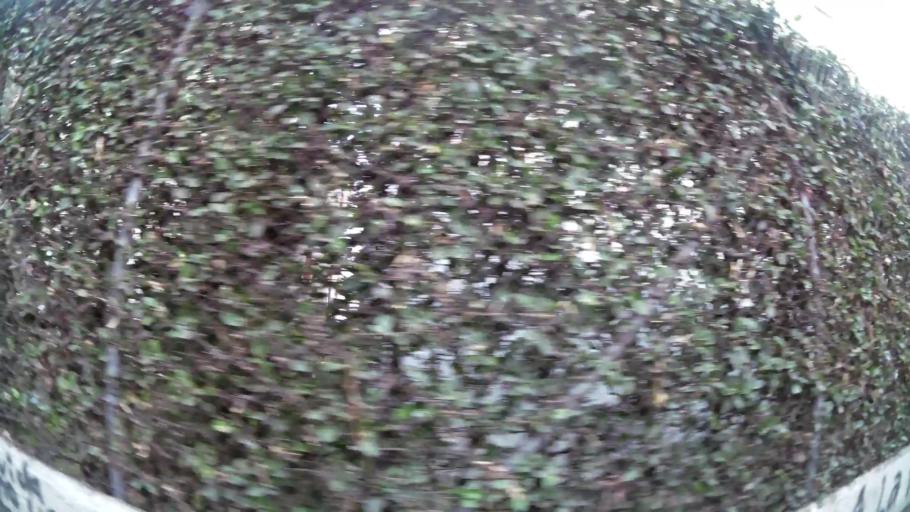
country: CO
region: Valle del Cauca
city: Cali
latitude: 3.4531
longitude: -76.4893
